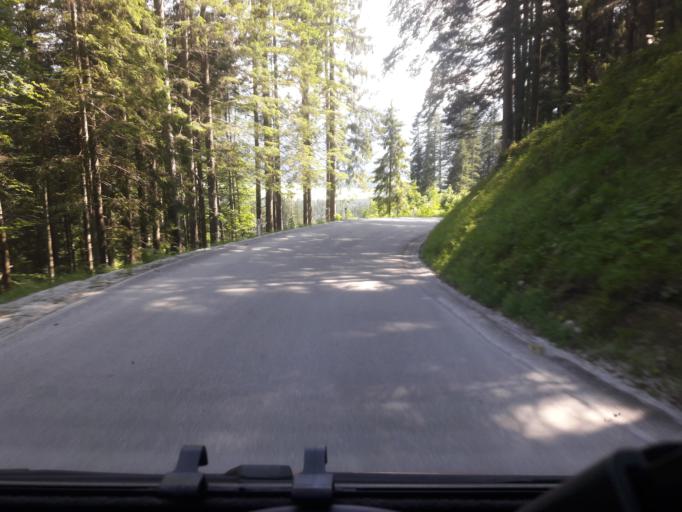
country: AT
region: Styria
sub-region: Politischer Bezirk Liezen
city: Tauplitz
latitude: 47.5728
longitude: 13.9622
